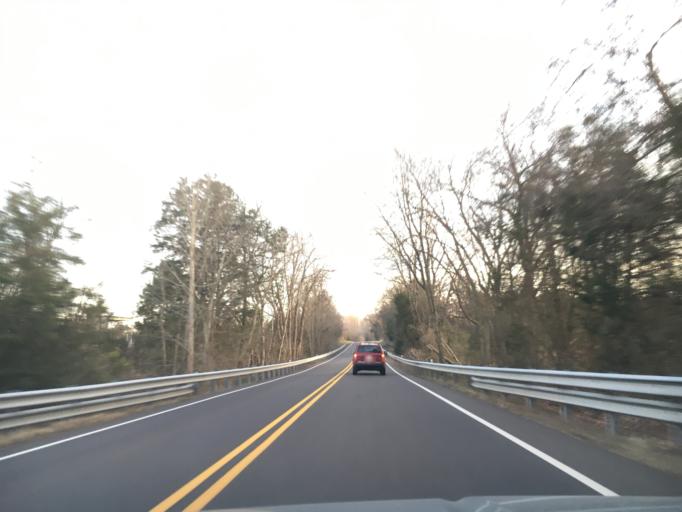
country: US
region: Virginia
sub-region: Louisa County
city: Louisa
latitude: 38.1377
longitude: -77.9232
